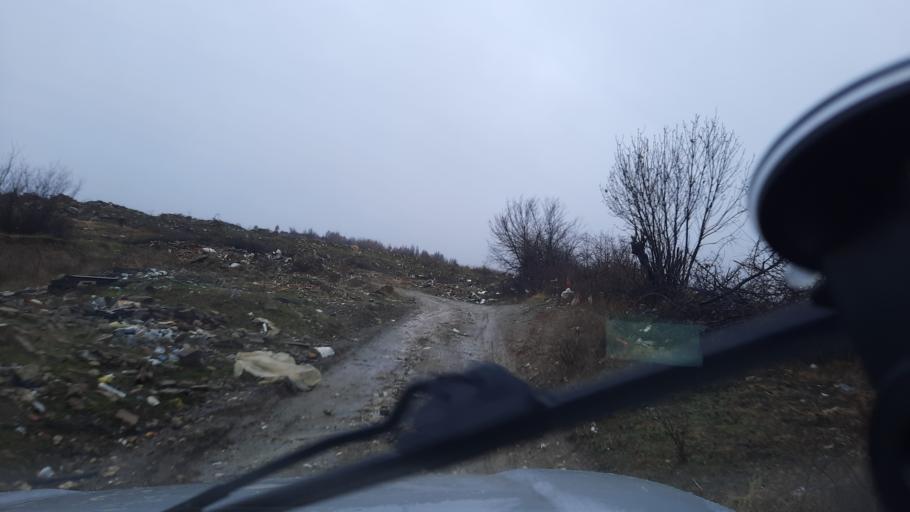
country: MK
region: Opstina Lipkovo
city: Matejche
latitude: 42.1253
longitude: 21.5856
